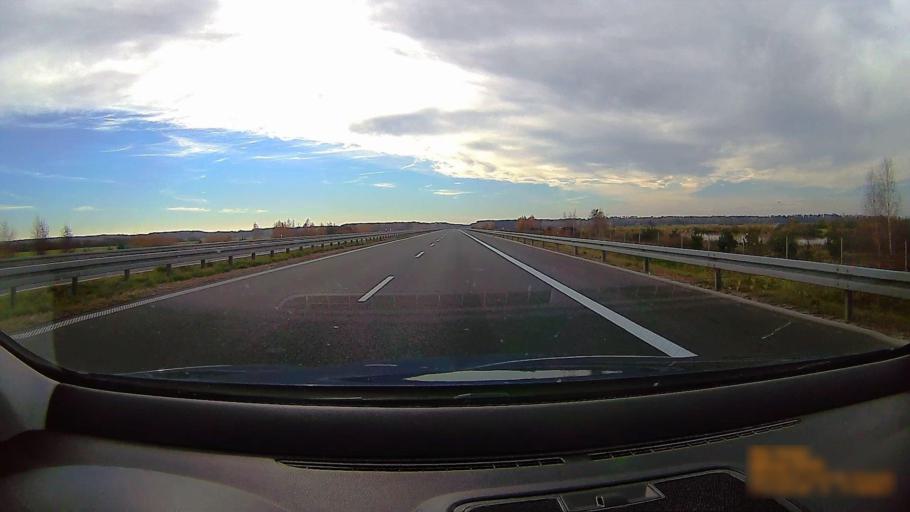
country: PL
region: Greater Poland Voivodeship
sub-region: Powiat ostrowski
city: Przygodzice
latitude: 51.5835
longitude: 17.8497
